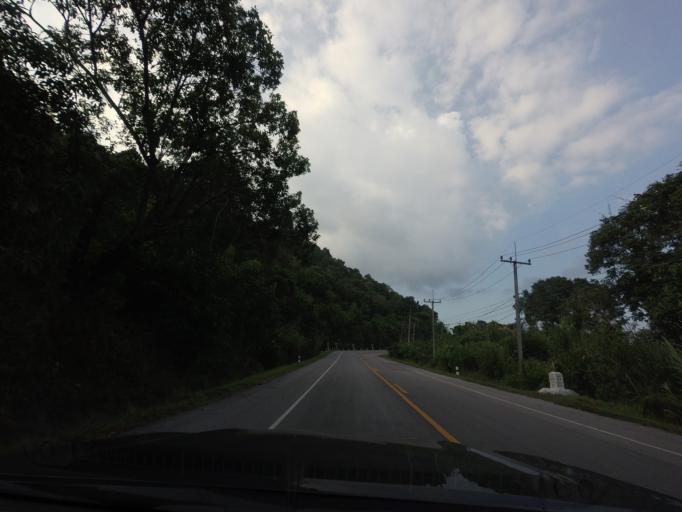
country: TH
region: Loei
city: Dan Sai
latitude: 17.3163
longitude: 101.1229
